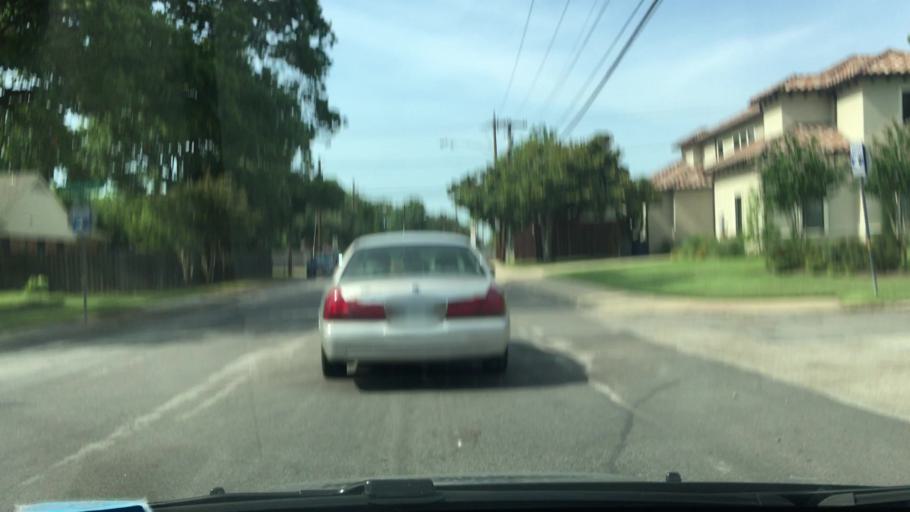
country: US
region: Texas
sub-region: Dallas County
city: Addison
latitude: 32.9175
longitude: -96.8116
